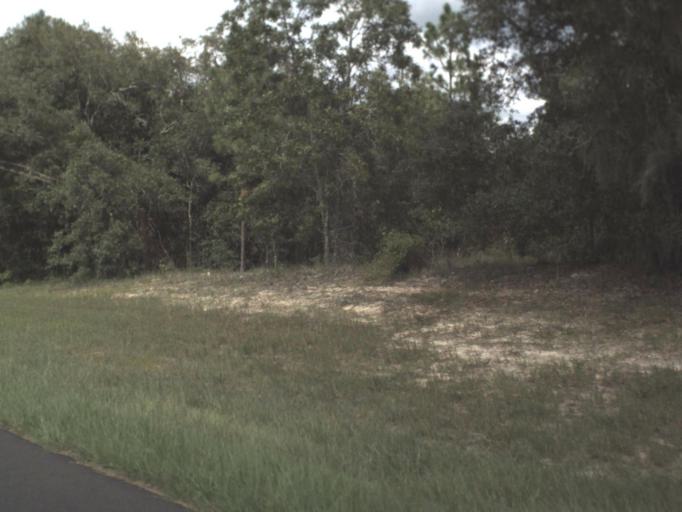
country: US
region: Florida
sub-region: Citrus County
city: Floral City
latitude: 28.7002
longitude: -82.3152
